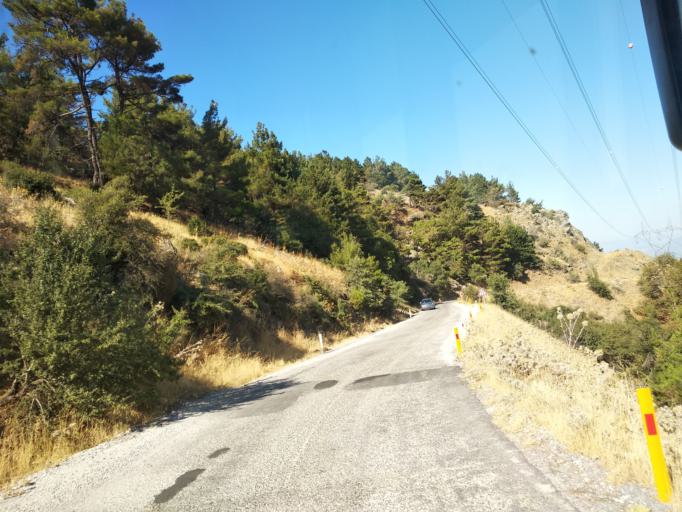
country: TR
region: Izmir
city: Gaziemir
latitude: 38.3146
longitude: 27.0060
